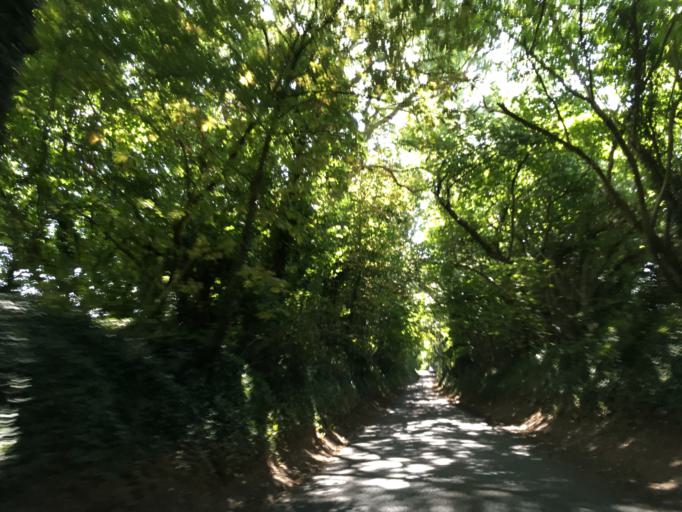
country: GB
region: England
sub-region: Hampshire
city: Colden Common
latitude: 51.0233
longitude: -1.2729
